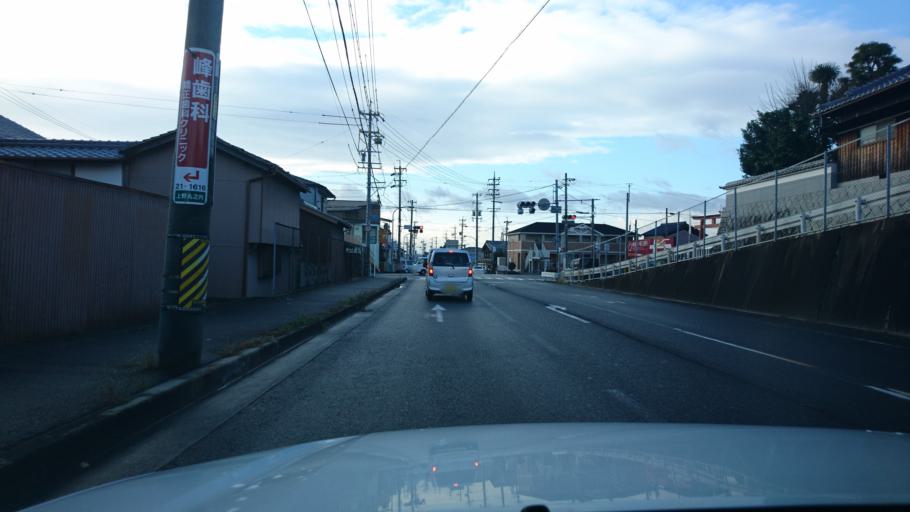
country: JP
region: Mie
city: Ueno-ebisumachi
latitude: 34.7678
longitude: 136.1233
